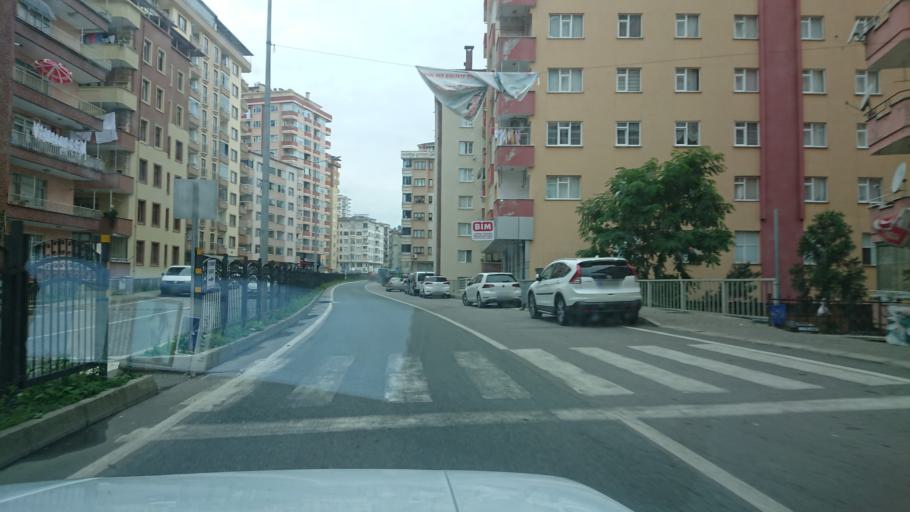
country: TR
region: Rize
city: Rize
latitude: 41.0235
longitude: 40.5393
